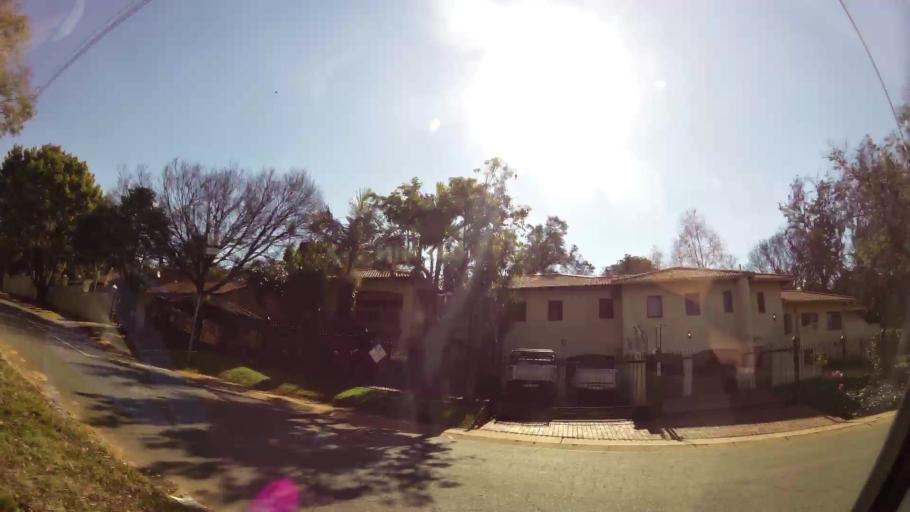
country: ZA
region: Gauteng
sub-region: City of Tshwane Metropolitan Municipality
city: Pretoria
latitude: -25.7601
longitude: 28.2703
